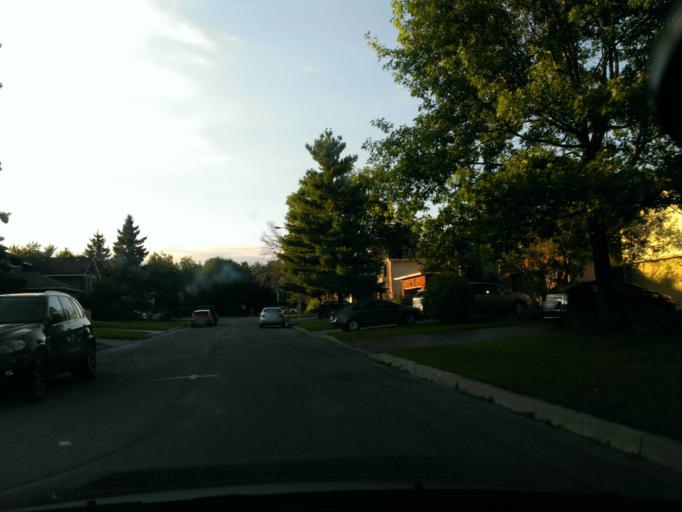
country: CA
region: Quebec
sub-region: Outaouais
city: Gatineau
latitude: 45.4837
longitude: -75.4951
